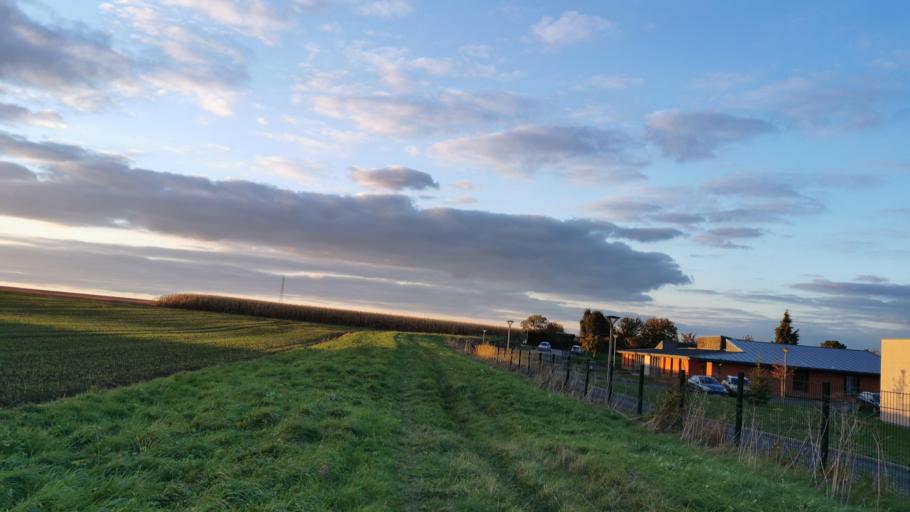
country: FR
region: Ile-de-France
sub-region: Departement des Yvelines
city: Plaisir
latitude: 48.8239
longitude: 1.9355
